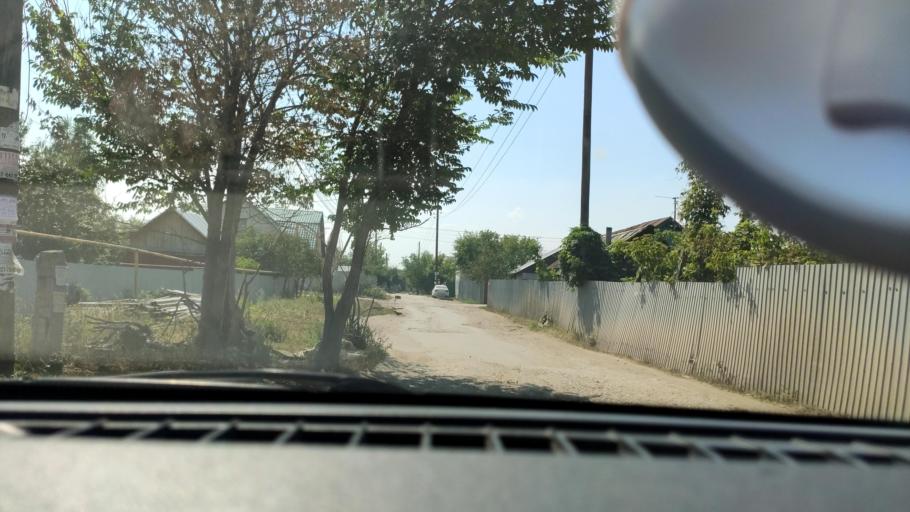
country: RU
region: Samara
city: Samara
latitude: 53.1413
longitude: 50.0966
